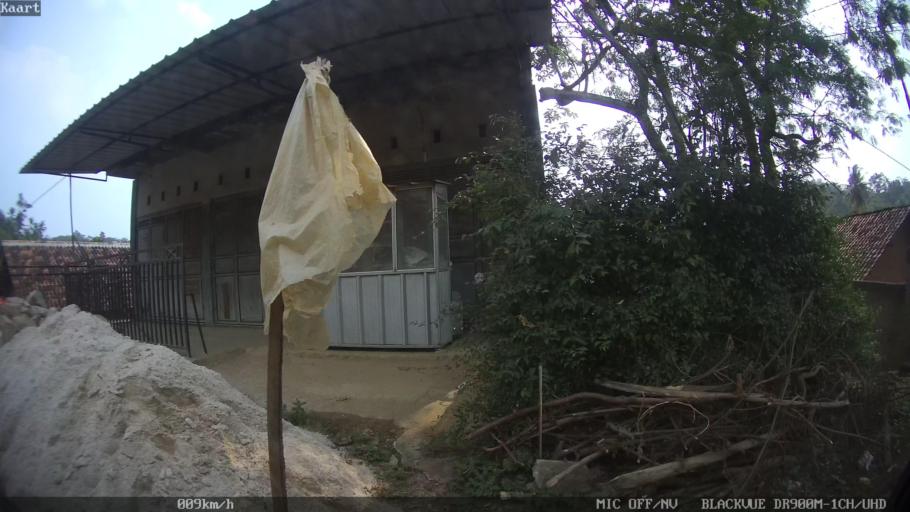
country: ID
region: Lampung
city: Gadingrejo
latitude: -5.3896
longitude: 105.0200
